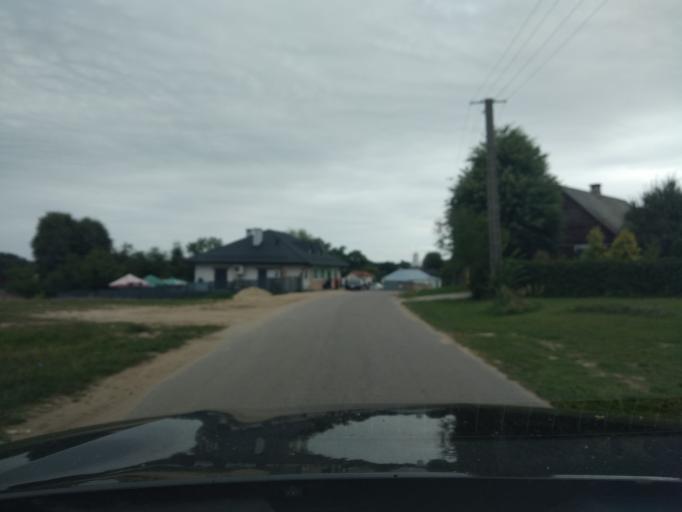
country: PL
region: Masovian Voivodeship
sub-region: Powiat pultuski
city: Obryte
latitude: 52.7542
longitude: 21.2086
